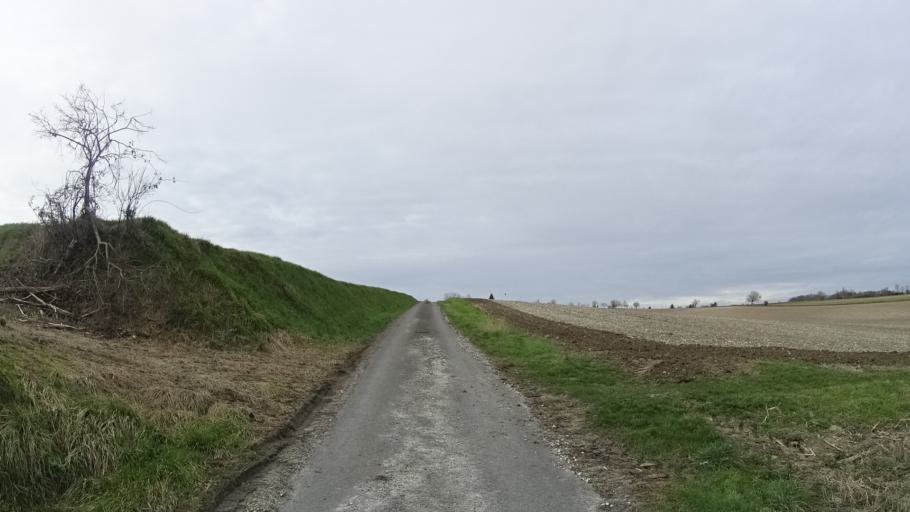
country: FR
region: Aquitaine
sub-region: Departement de la Dordogne
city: Saint-Aulaye
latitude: 45.2574
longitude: 0.1641
